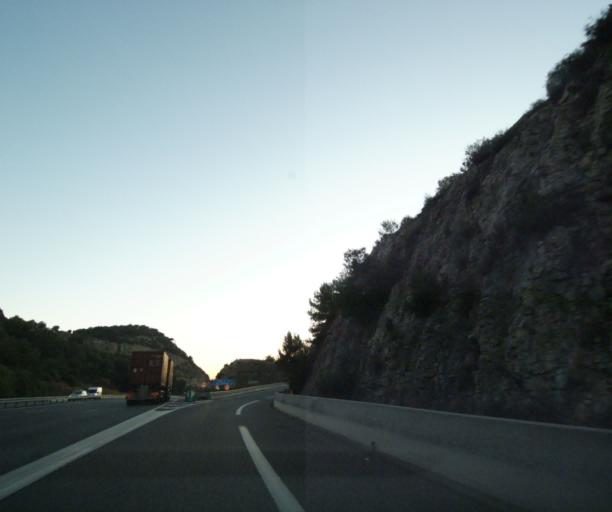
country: FR
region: Provence-Alpes-Cote d'Azur
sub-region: Departement des Bouches-du-Rhone
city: Roquefort-la-Bedoule
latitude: 43.2384
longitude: 5.5912
